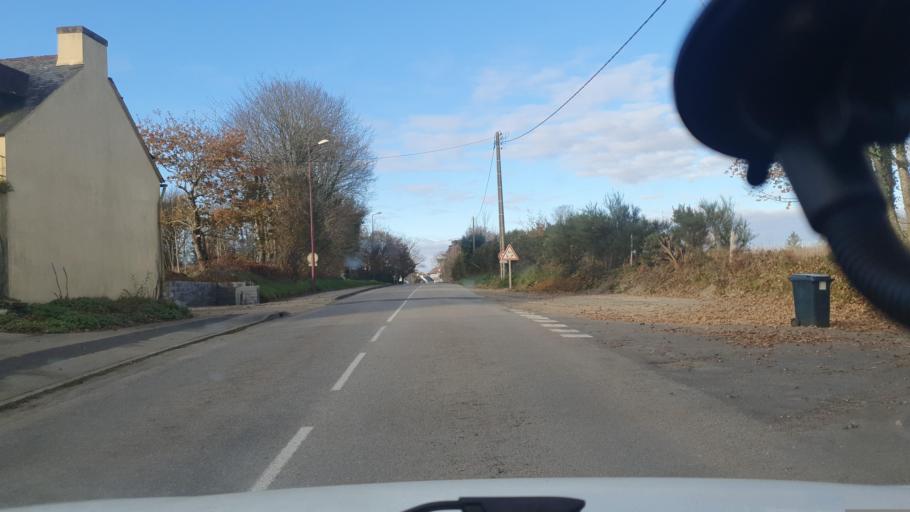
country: FR
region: Brittany
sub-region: Departement du Finistere
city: Briec
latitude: 48.0937
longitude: -3.9947
